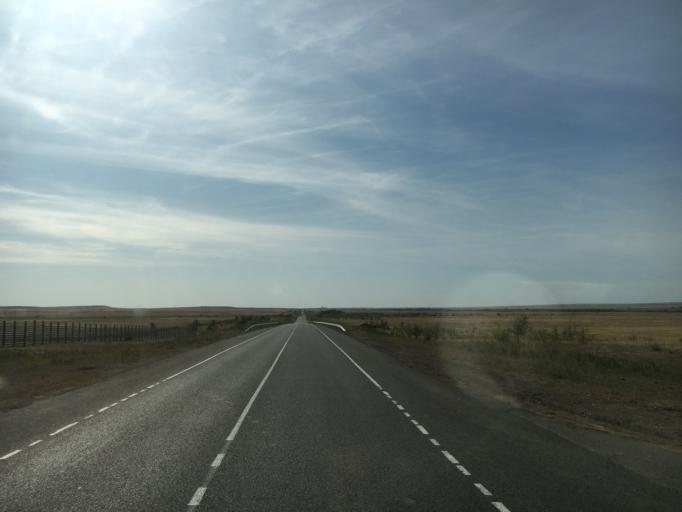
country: KZ
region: Batys Qazaqstan
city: Kamenka
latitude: 51.1083
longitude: 50.4367
